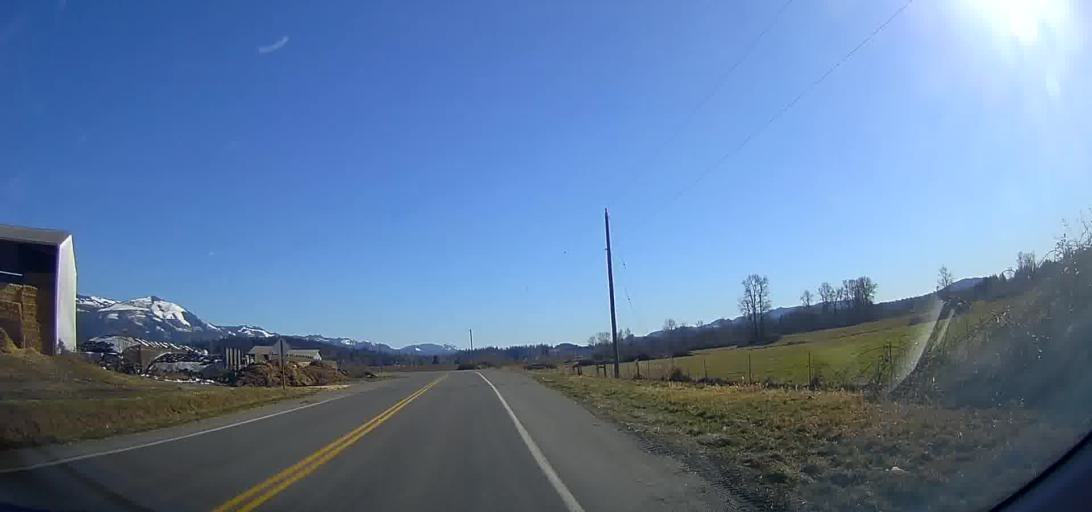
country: US
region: Washington
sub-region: Skagit County
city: Clear Lake
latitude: 48.4662
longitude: -122.2740
